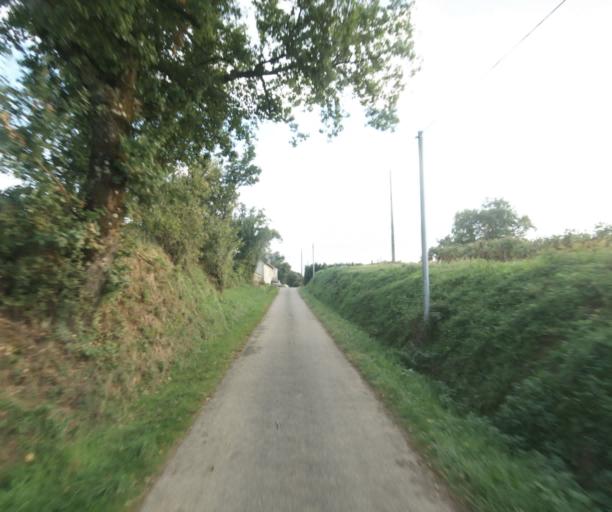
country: FR
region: Midi-Pyrenees
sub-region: Departement du Gers
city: Le Houga
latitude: 43.8359
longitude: -0.1088
